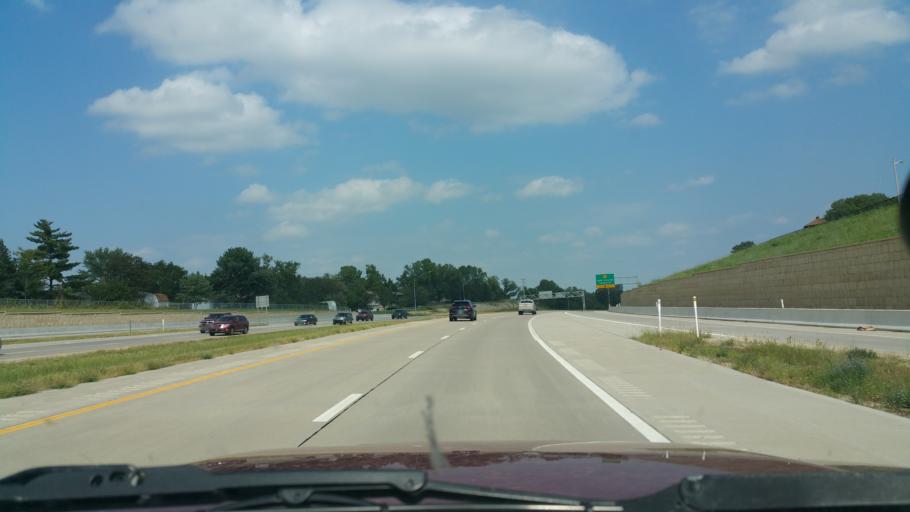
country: US
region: Kansas
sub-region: Riley County
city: Manhattan
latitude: 39.1678
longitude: -96.6144
